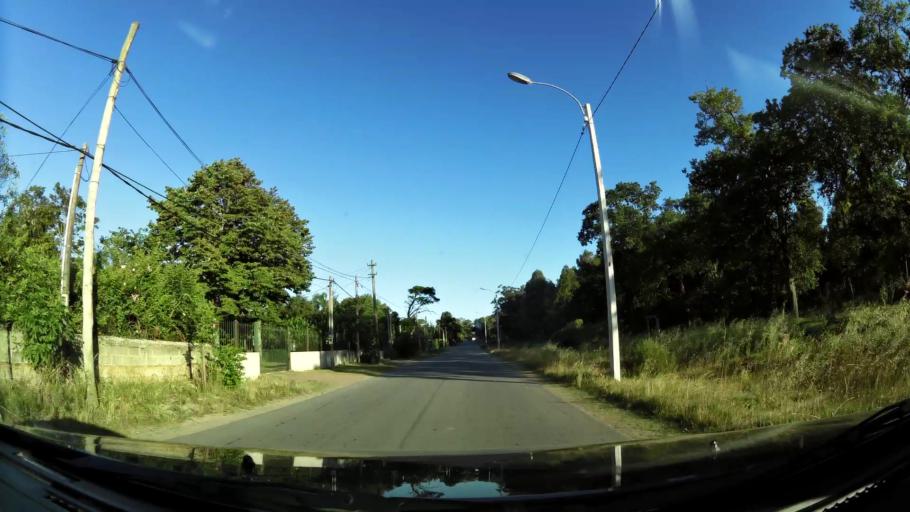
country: UY
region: Canelones
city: Paso de Carrasco
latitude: -34.8498
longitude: -56.0302
